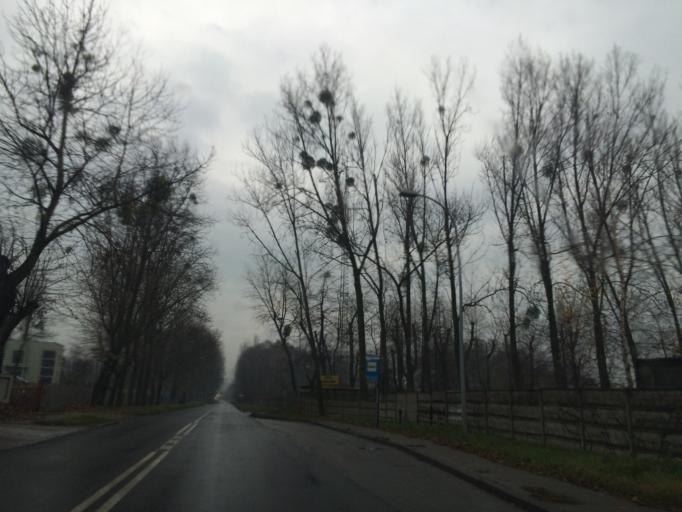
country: PL
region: Silesian Voivodeship
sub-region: Piekary Slaskie
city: Piekary Slaskie
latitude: 50.3761
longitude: 18.9093
